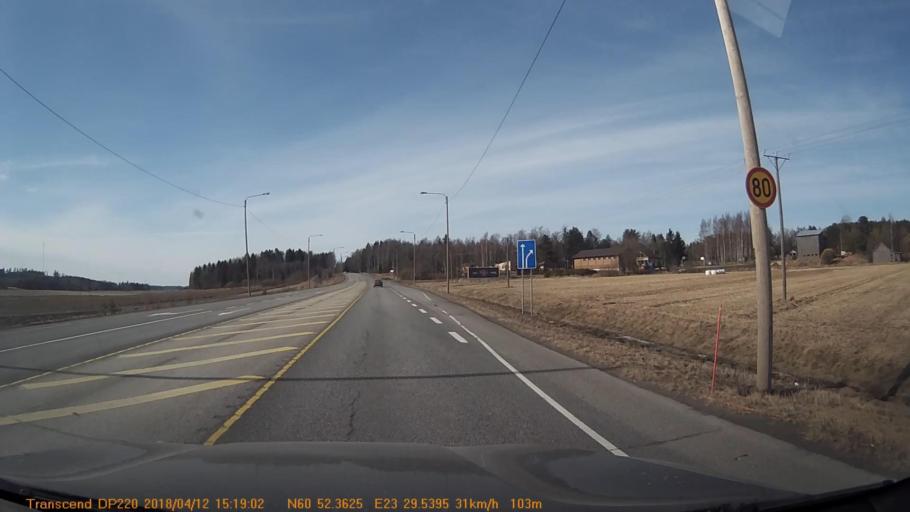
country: FI
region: Haeme
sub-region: Forssa
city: Jokioinen
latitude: 60.8732
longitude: 23.4915
